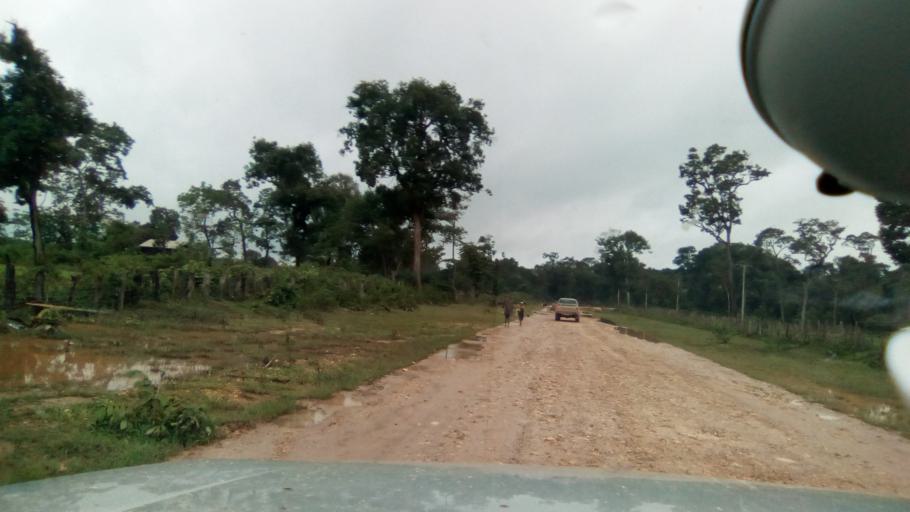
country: LA
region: Attapu
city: Attapu
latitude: 14.6754
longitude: 106.5652
